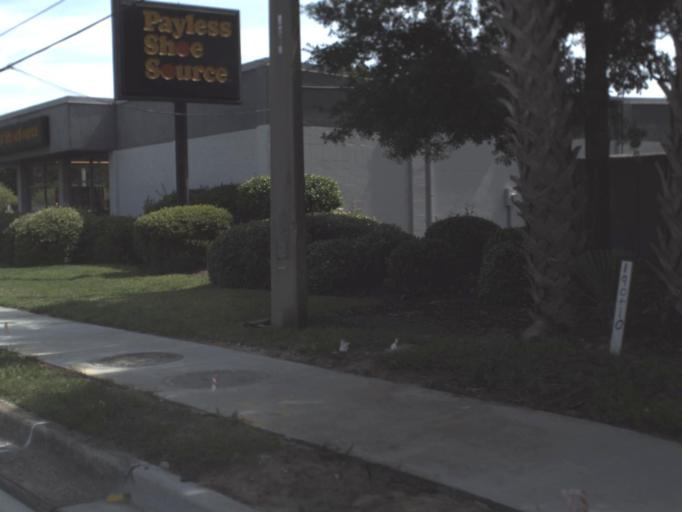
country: US
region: Florida
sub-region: Duval County
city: Jacksonville
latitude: 30.2840
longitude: -81.6027
